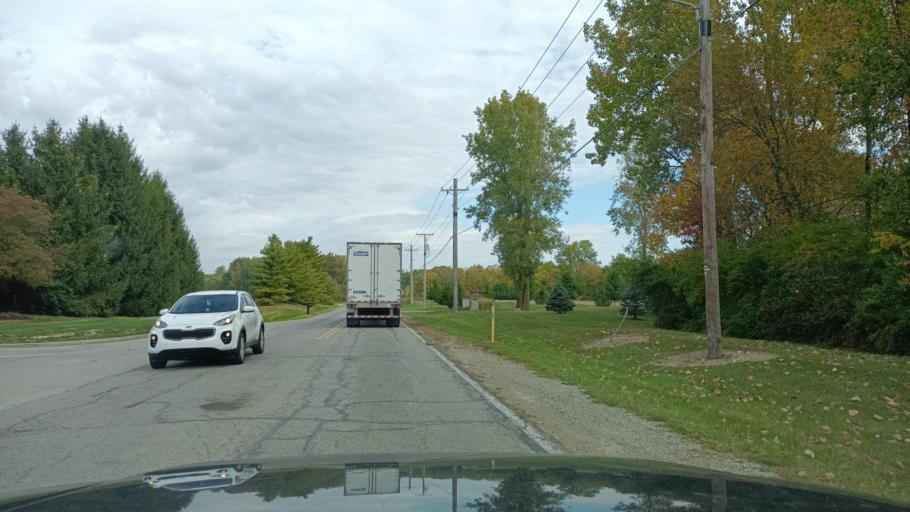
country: US
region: Indiana
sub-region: Delaware County
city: Yorktown
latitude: 40.1910
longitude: -85.4617
